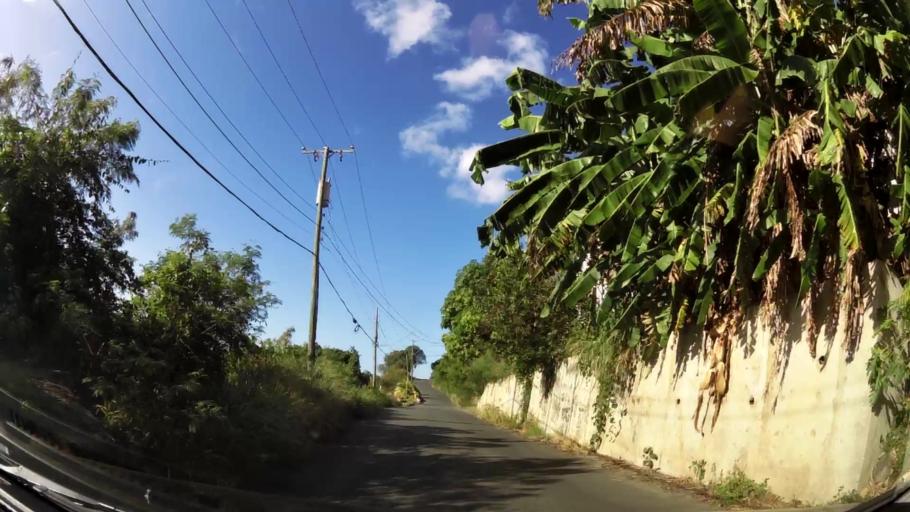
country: VG
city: Road Town
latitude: 18.4187
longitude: -64.6631
